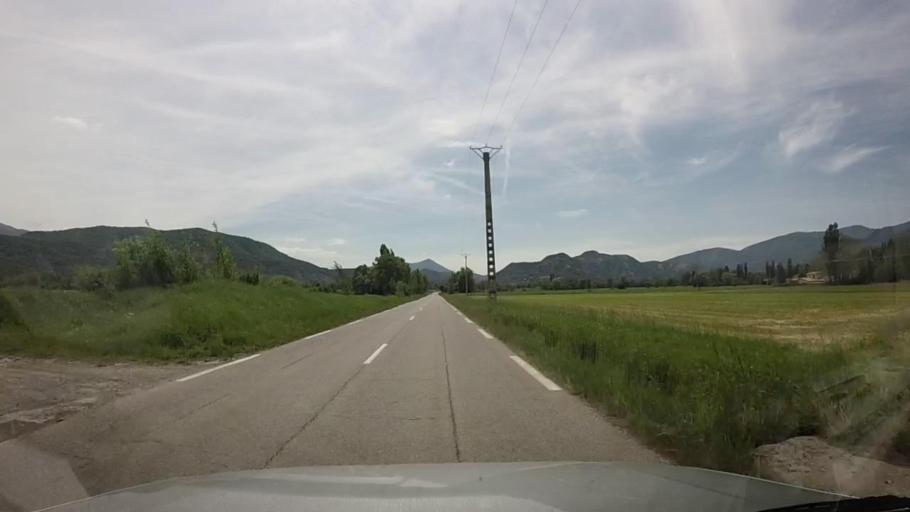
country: FR
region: Provence-Alpes-Cote d'Azur
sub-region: Departement des Alpes-de-Haute-Provence
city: Le Brusquet
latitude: 44.1447
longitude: 6.2952
